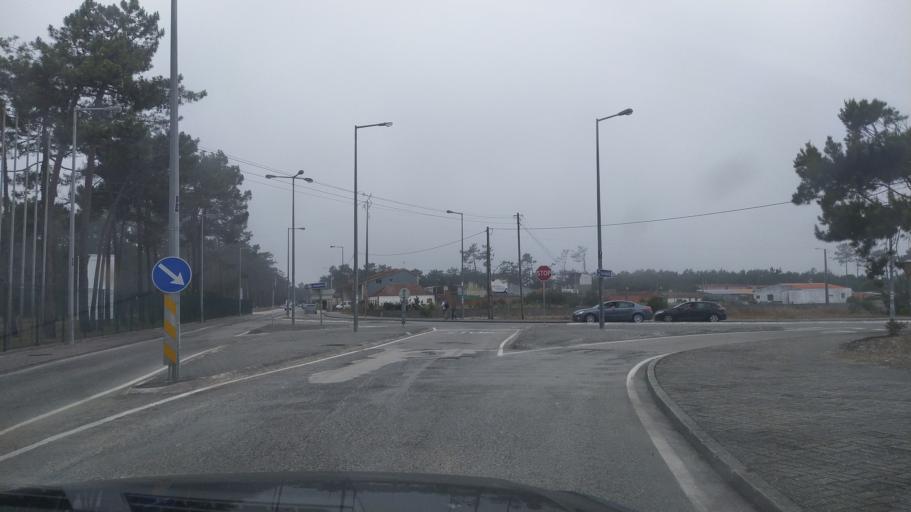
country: PT
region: Aveiro
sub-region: Ilhavo
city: Gafanha da Encarnacao
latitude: 40.5578
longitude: -8.7455
